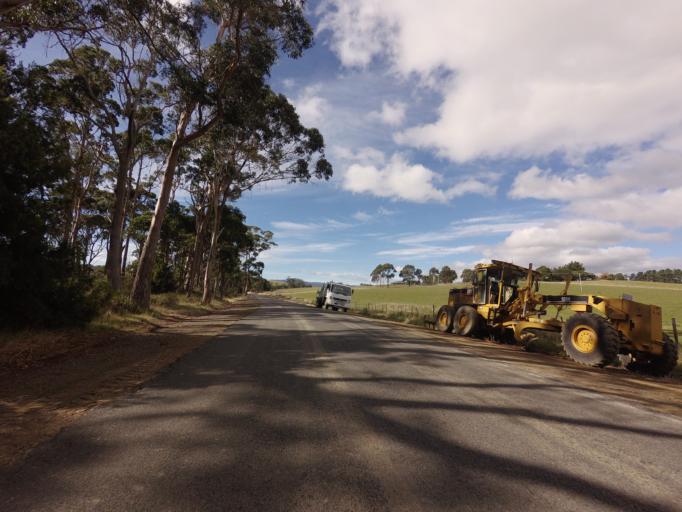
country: AU
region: Tasmania
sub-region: Clarence
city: Sandford
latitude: -43.0445
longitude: 147.7492
